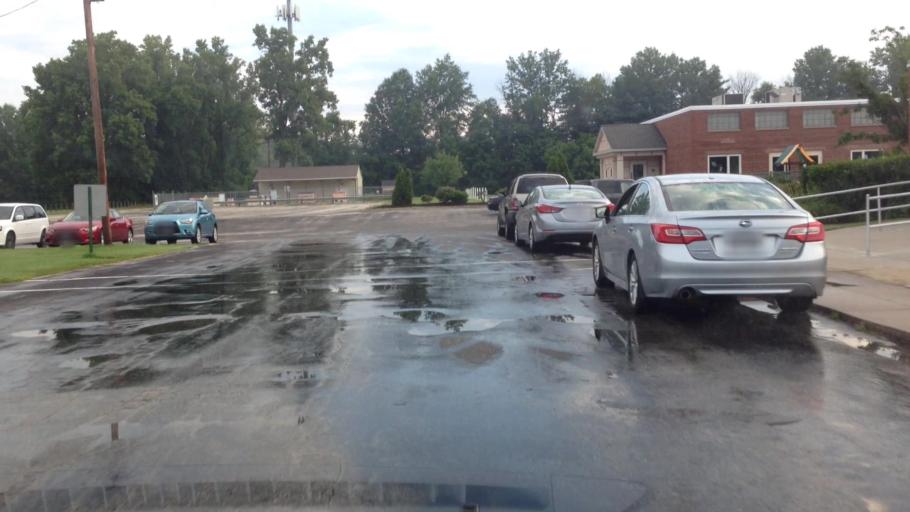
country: US
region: Ohio
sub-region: Cuyahoga County
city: Olmsted Falls
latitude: 41.3732
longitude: -81.9117
